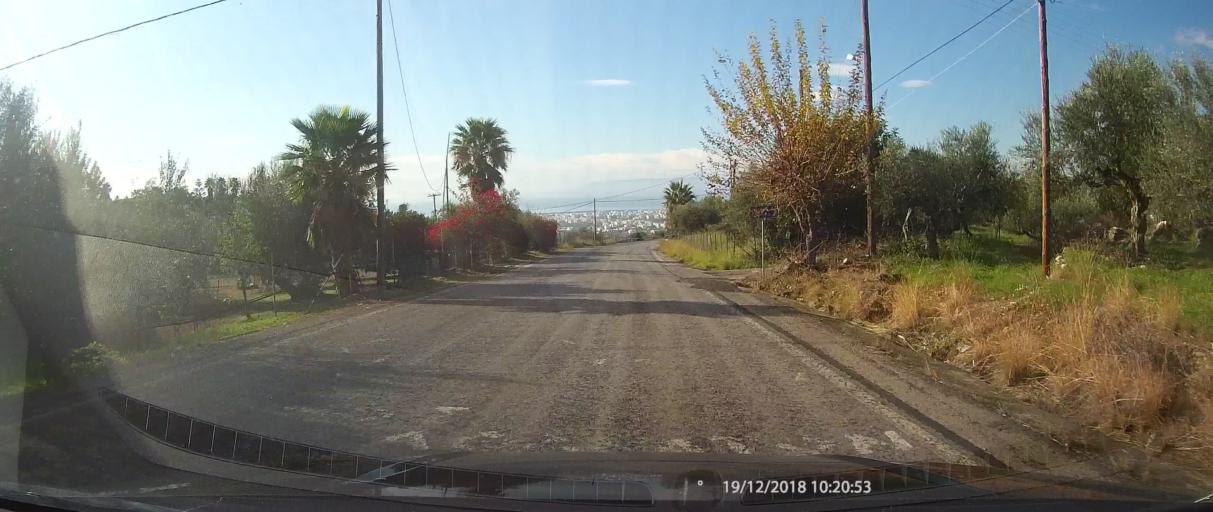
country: GR
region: Peloponnese
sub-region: Nomos Messinias
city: Kalamata
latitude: 37.0499
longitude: 22.1375
